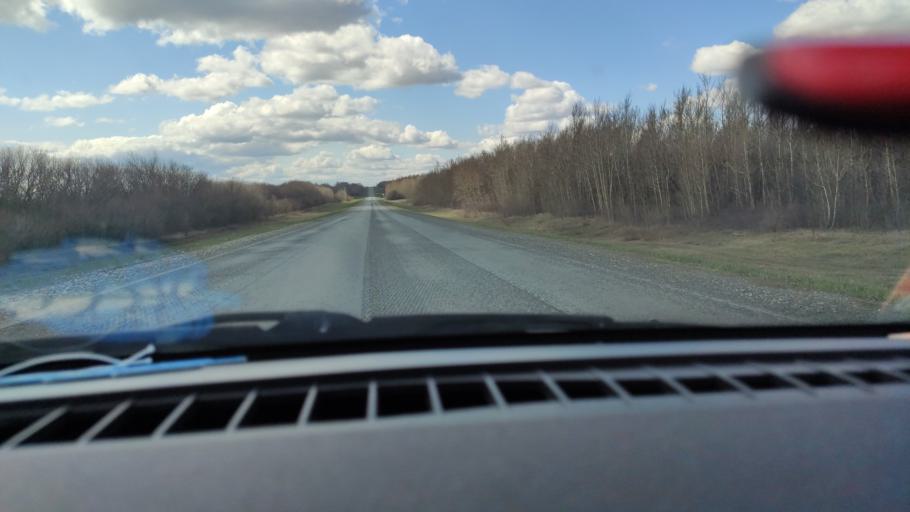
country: RU
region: Saratov
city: Dukhovnitskoye
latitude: 52.6939
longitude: 48.2470
